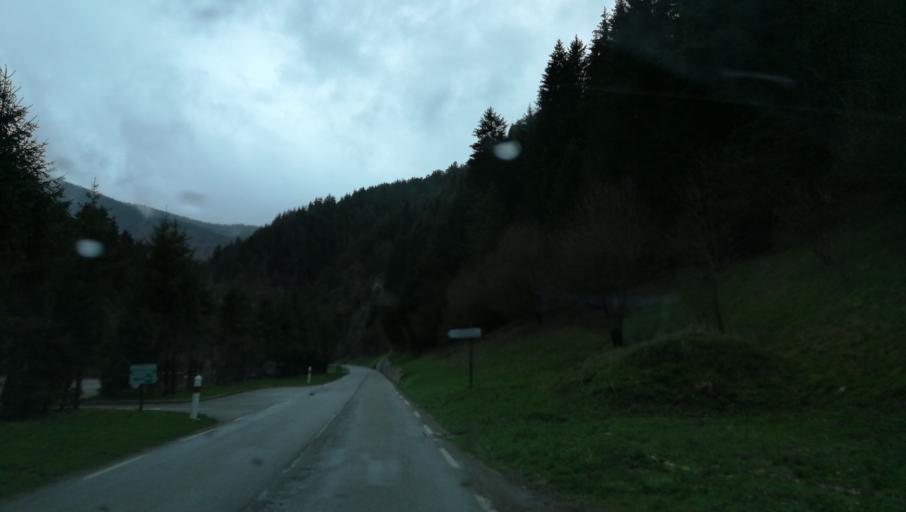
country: FR
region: Rhone-Alpes
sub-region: Departement de l'Isere
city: Villard-de-Lans
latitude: 45.0821
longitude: 5.5327
